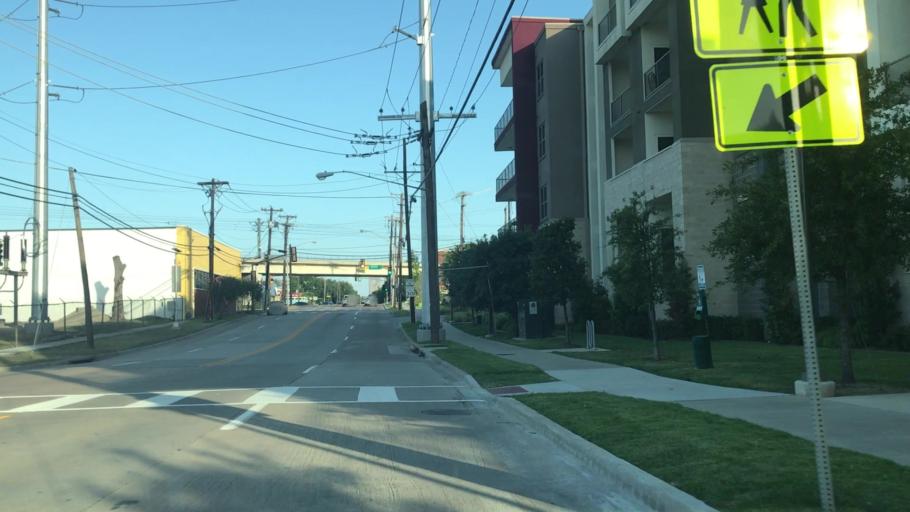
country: US
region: Texas
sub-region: Dallas County
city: Highland Park
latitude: 32.8194
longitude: -96.8342
